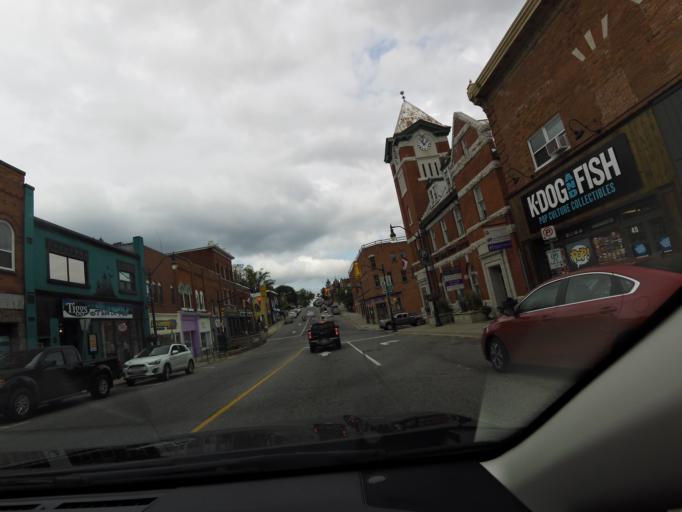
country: CA
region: Ontario
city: Bracebridge
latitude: 45.0411
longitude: -79.3102
